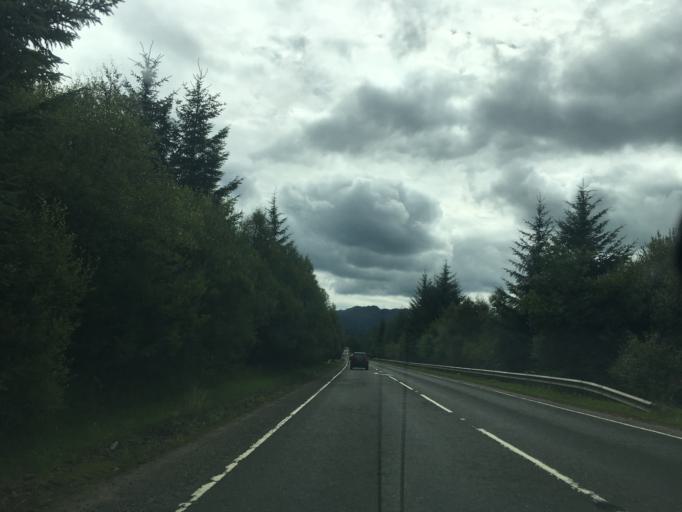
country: GB
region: Scotland
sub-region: Stirling
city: Callander
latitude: 56.3490
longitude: -4.3282
